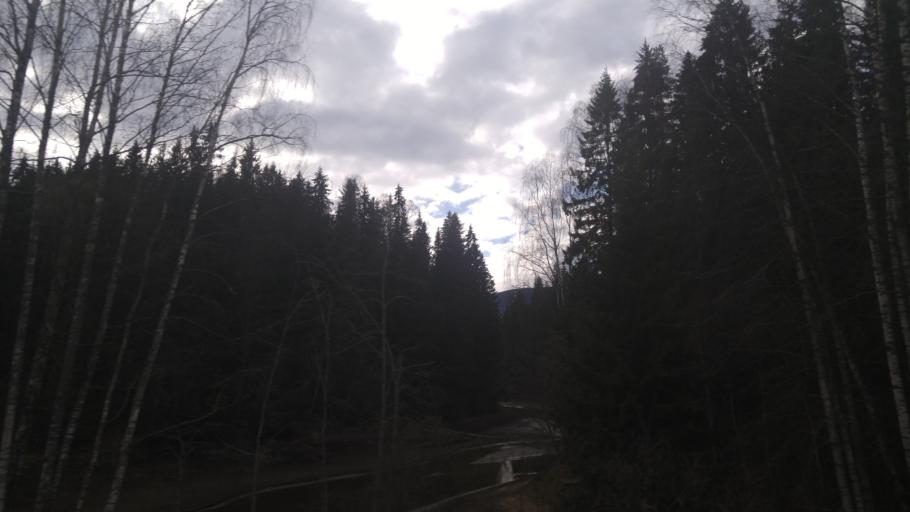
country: NO
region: Akershus
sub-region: Eidsvoll
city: Eidsvoll
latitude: 60.3713
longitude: 11.2425
